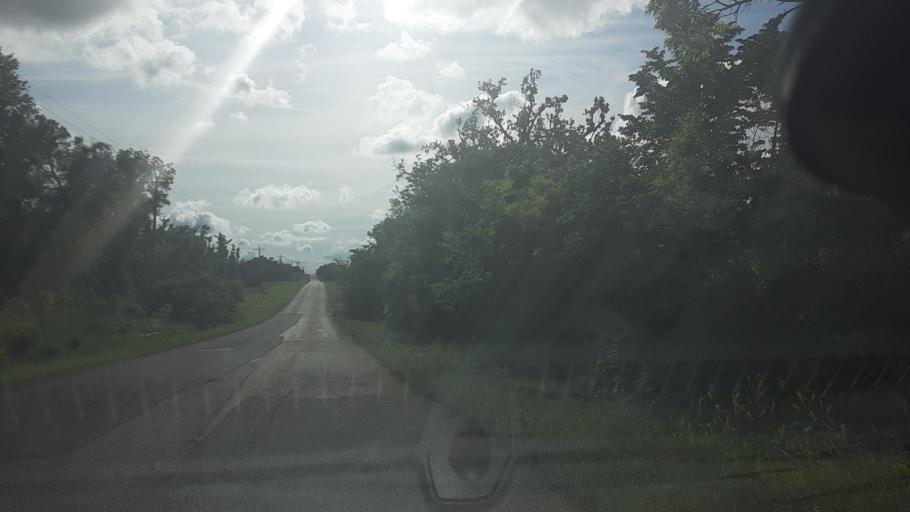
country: US
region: Oklahoma
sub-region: Logan County
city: Langston
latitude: 36.0579
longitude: -97.3675
